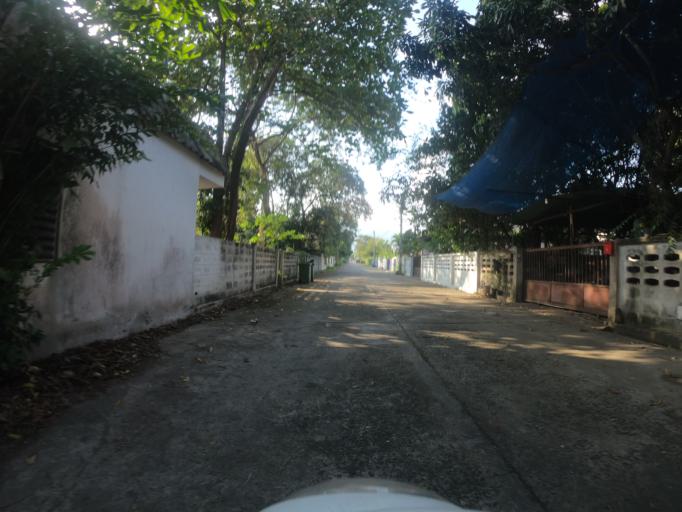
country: TH
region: Chiang Mai
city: Chiang Mai
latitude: 18.8164
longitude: 98.9763
